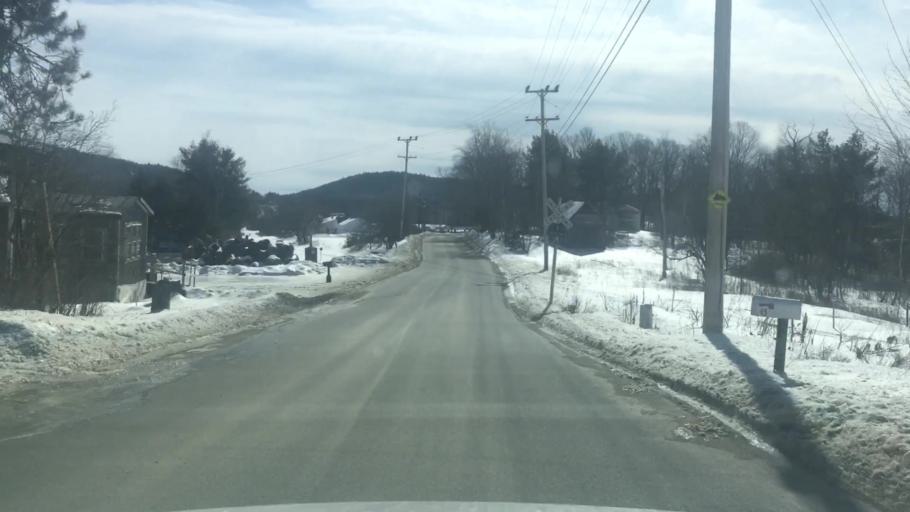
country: US
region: Maine
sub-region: Penobscot County
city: Holden
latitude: 44.7400
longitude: -68.6288
